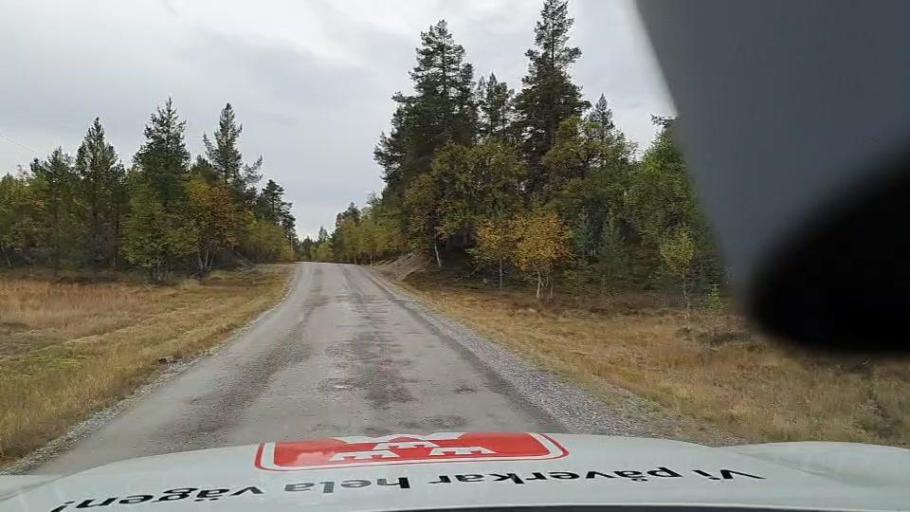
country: NO
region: Hedmark
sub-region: Engerdal
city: Engerdal
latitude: 62.0869
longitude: 12.7512
